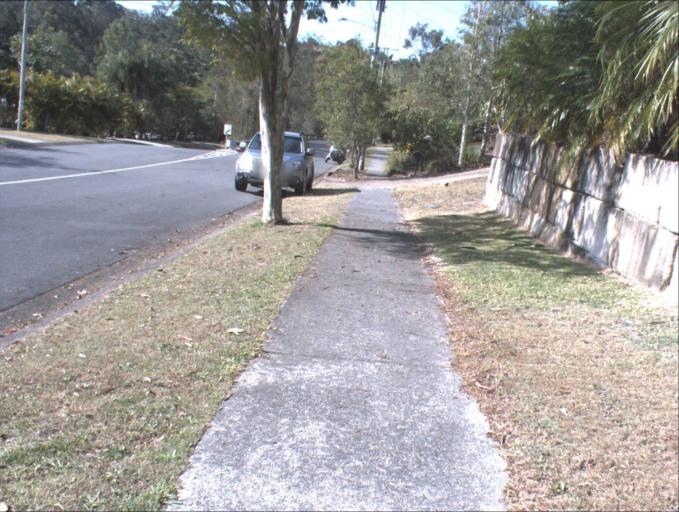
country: AU
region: Queensland
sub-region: Logan
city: Slacks Creek
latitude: -27.6580
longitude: 153.1830
